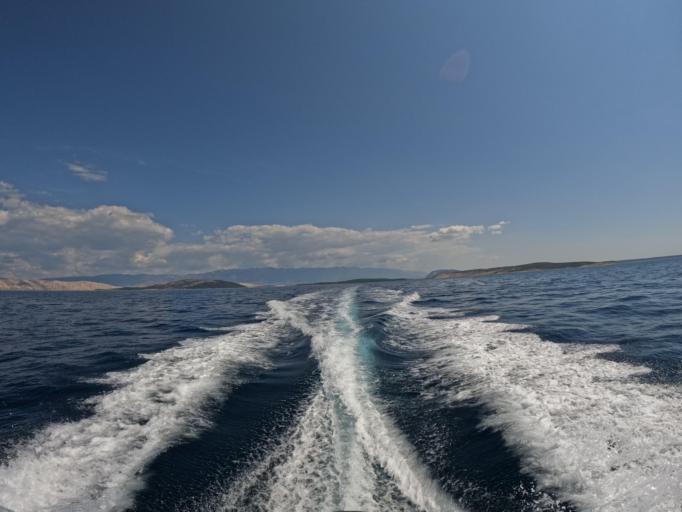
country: HR
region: Primorsko-Goranska
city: Lopar
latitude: 44.8707
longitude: 14.6733
